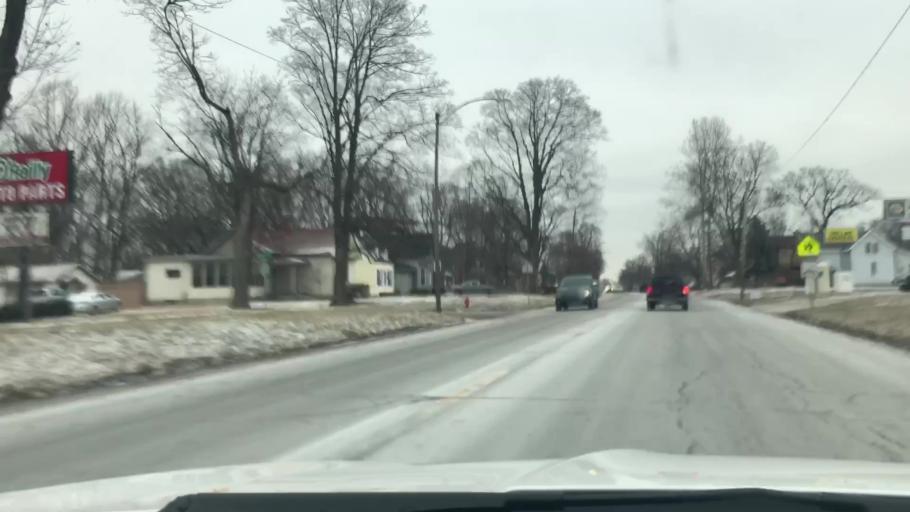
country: US
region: Indiana
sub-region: Fulton County
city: Rochester
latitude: 41.0578
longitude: -86.2169
